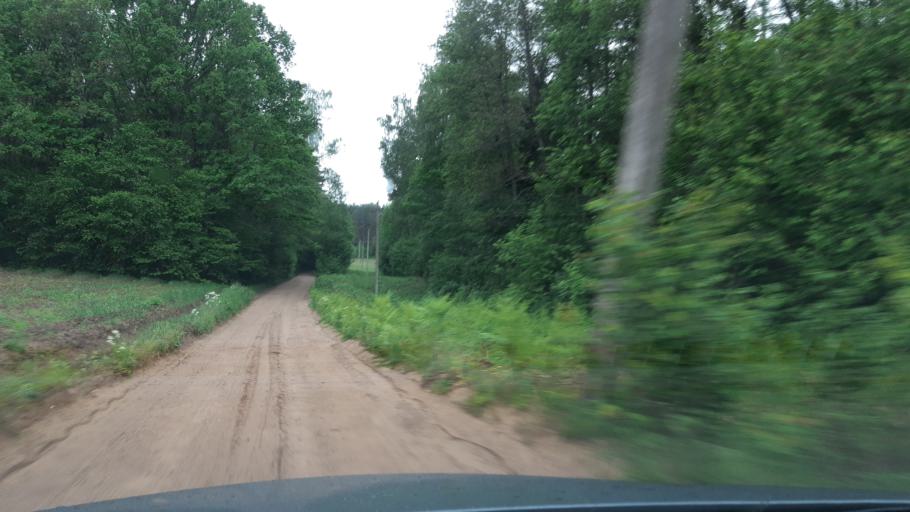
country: LT
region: Utenos apskritis
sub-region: Anyksciai
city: Anyksciai
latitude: 55.4506
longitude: 25.2116
